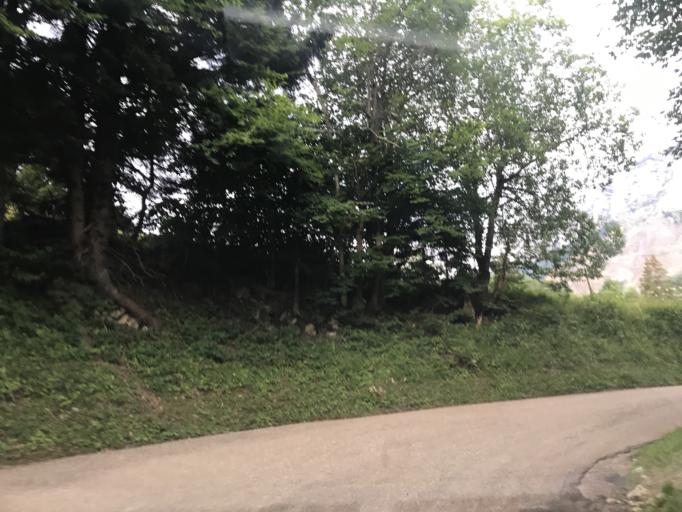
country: FR
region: Rhone-Alpes
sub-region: Departement de l'Isere
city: Saint-Vincent-de-Mercuze
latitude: 45.3856
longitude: 5.9338
